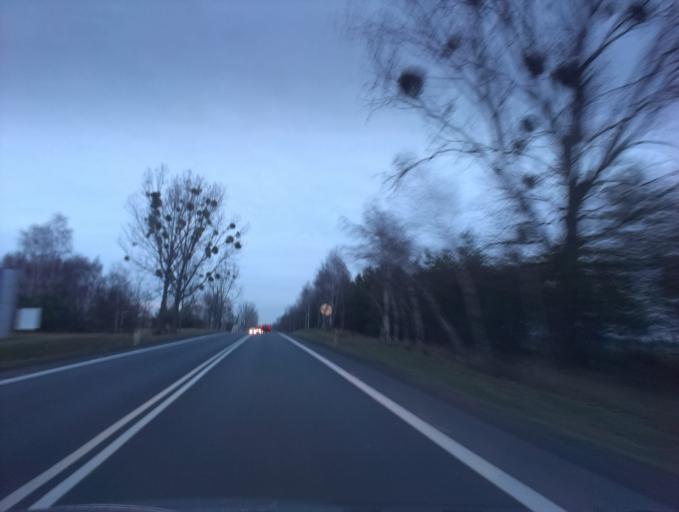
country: PL
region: Greater Poland Voivodeship
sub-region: Powiat poznanski
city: Zlotniki
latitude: 52.5376
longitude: 16.8367
